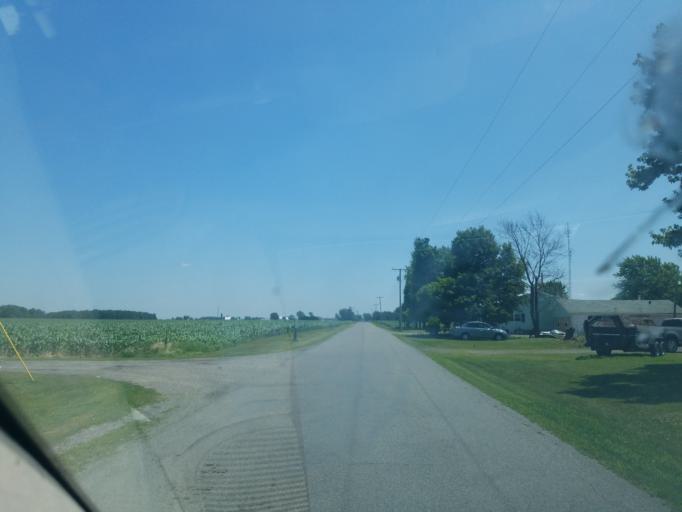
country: US
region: Ohio
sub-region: Allen County
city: Spencerville
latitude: 40.7575
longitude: -84.3820
